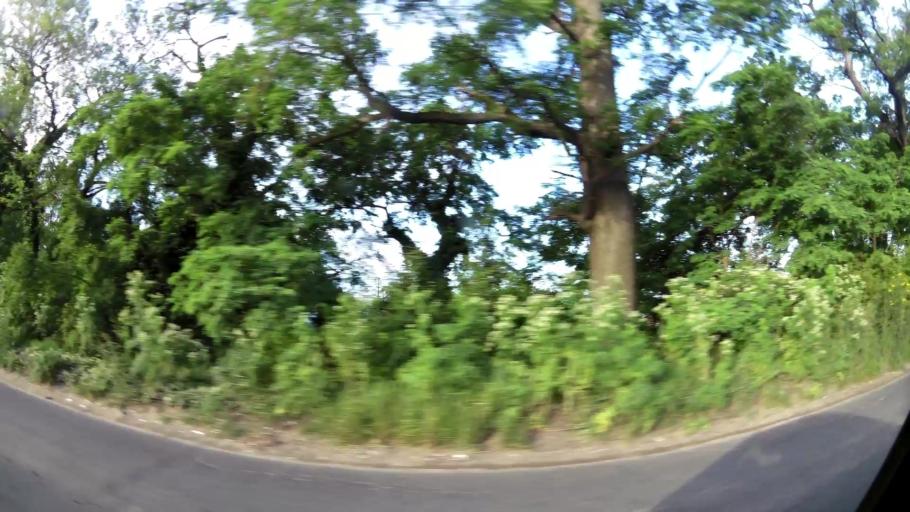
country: AR
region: Buenos Aires
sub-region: Partido de Quilmes
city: Quilmes
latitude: -34.8155
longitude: -58.2001
